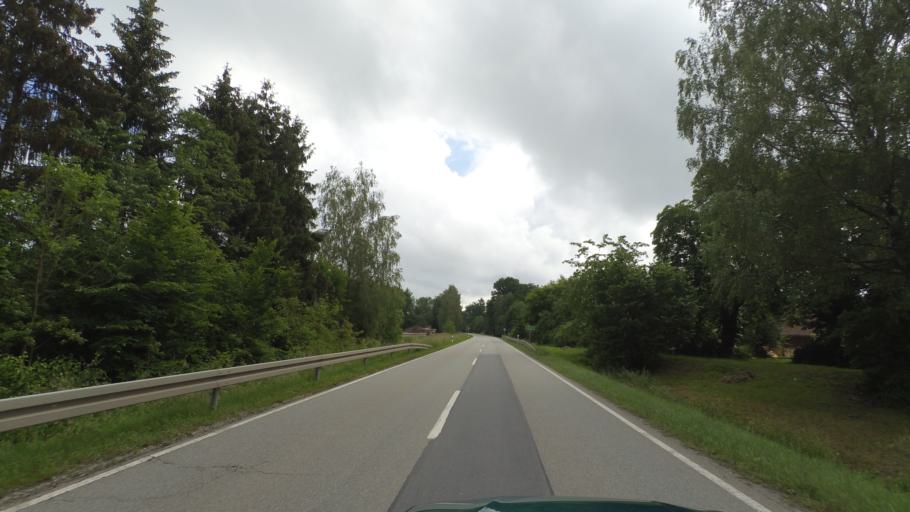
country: DE
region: Bavaria
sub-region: Lower Bavaria
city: Steinach
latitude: 48.9553
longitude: 12.6395
